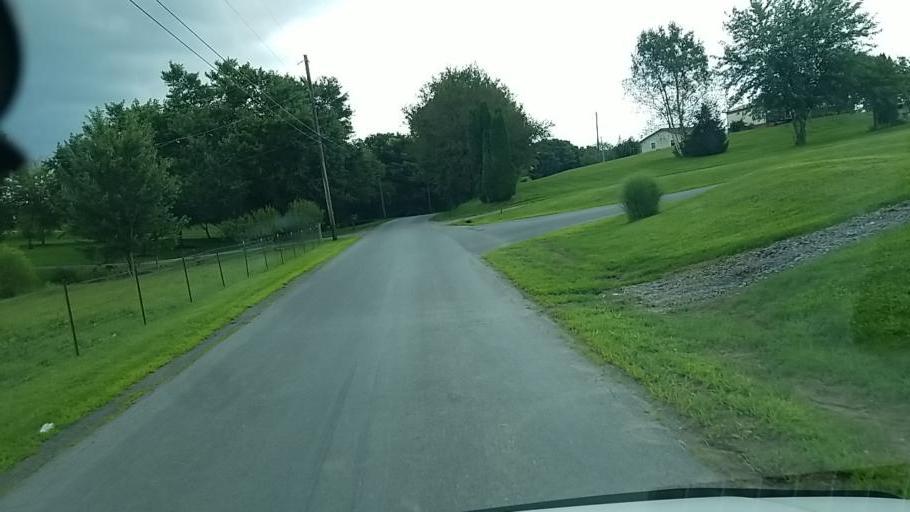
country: US
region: Pennsylvania
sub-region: Dauphin County
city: Elizabethville
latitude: 40.5917
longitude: -76.8259
